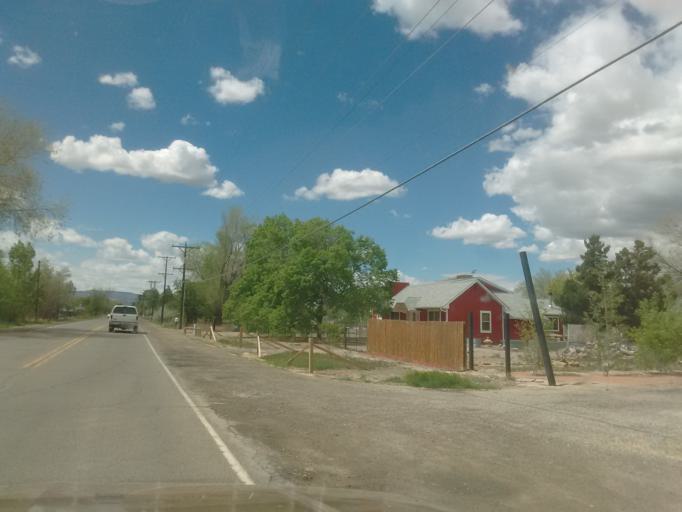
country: US
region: Colorado
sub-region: Mesa County
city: Fruitvale
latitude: 39.0773
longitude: -108.4710
